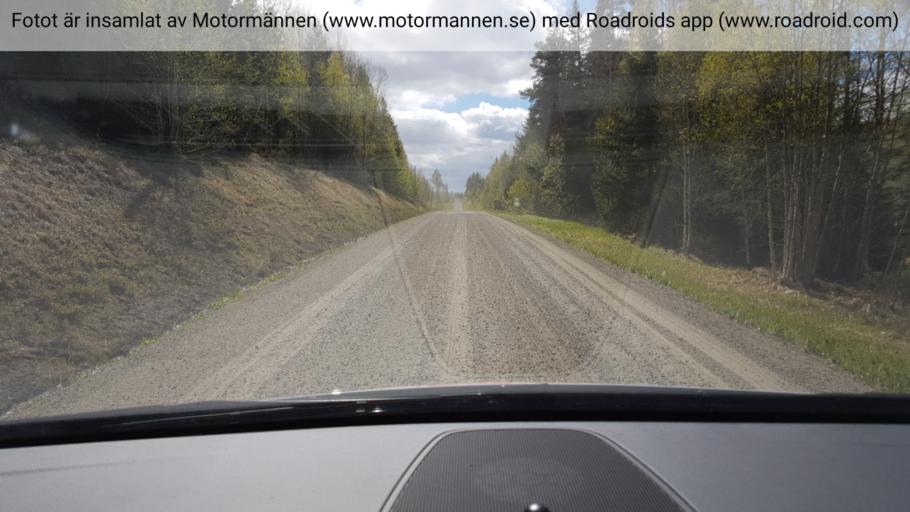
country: SE
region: Jaemtland
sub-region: OEstersunds Kommun
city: Brunflo
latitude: 62.9449
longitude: 14.9809
